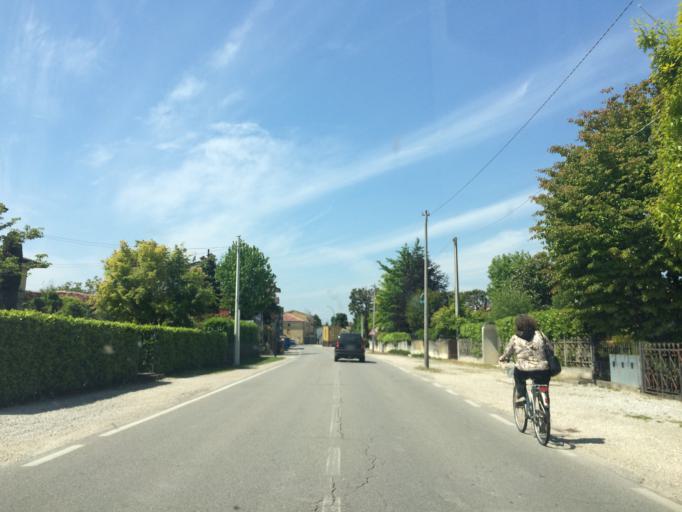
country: IT
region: Veneto
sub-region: Provincia di Padova
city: Fontaniva
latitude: 45.6321
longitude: 11.7592
